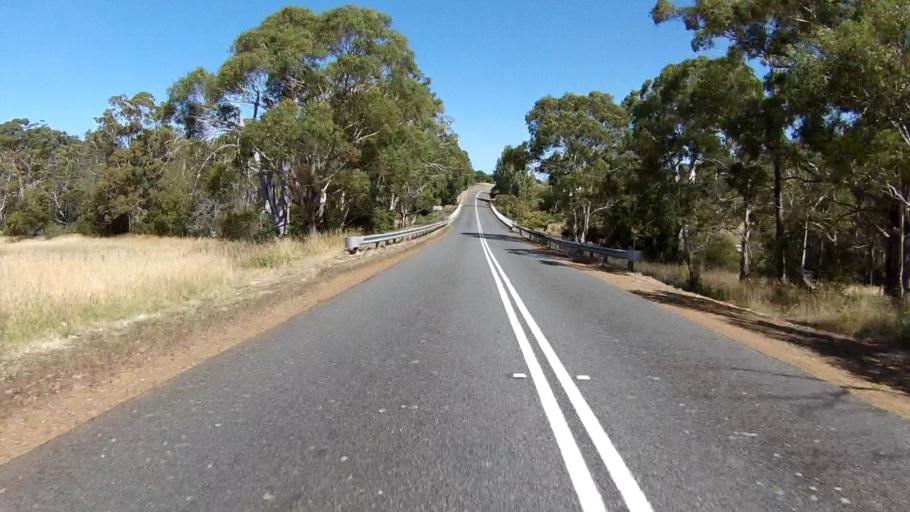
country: AU
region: Tasmania
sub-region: Sorell
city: Sorell
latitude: -42.2844
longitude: 147.9978
